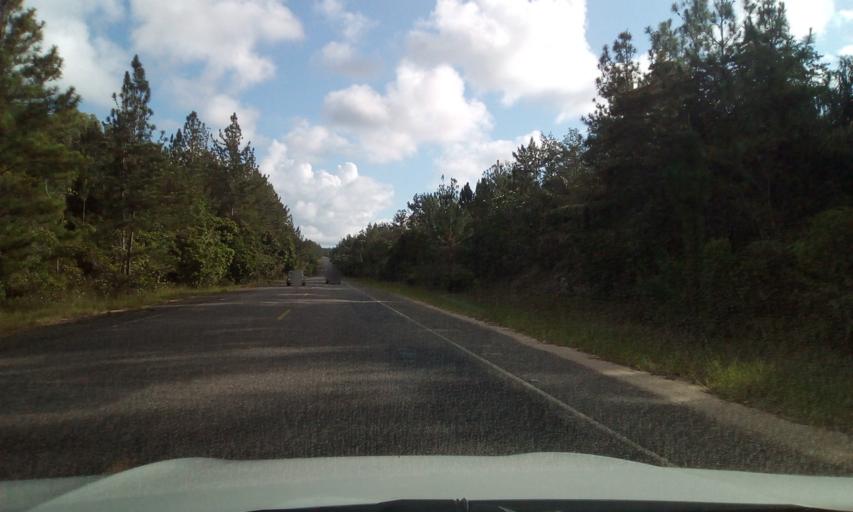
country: BR
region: Bahia
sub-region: Entre Rios
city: Entre Rios
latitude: -12.1493
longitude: -37.7984
